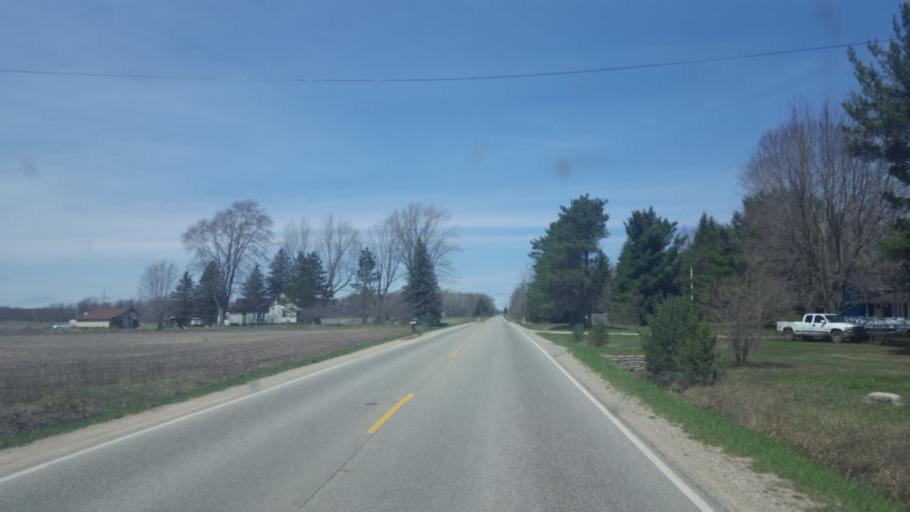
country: US
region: Michigan
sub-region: Gladwin County
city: Beaverton
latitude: 43.8799
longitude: -84.5857
